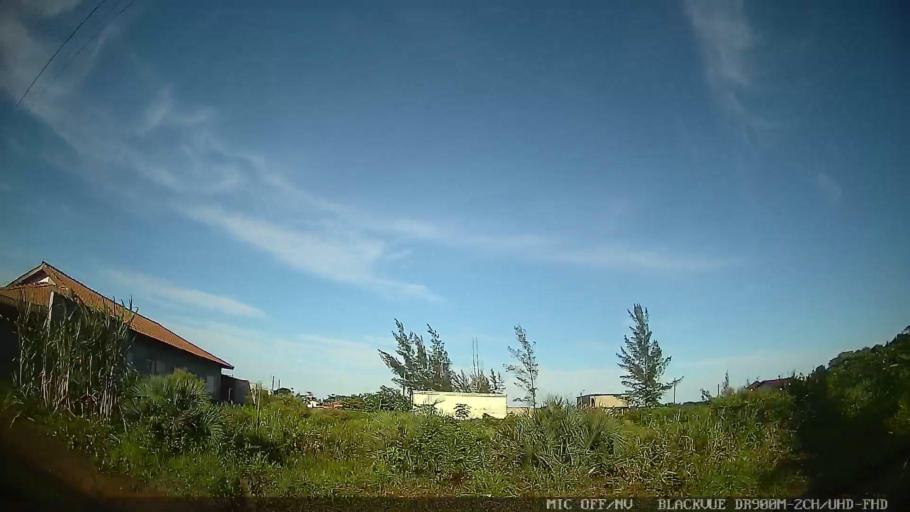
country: BR
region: Sao Paulo
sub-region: Iguape
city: Iguape
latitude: -24.7538
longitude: -47.5663
